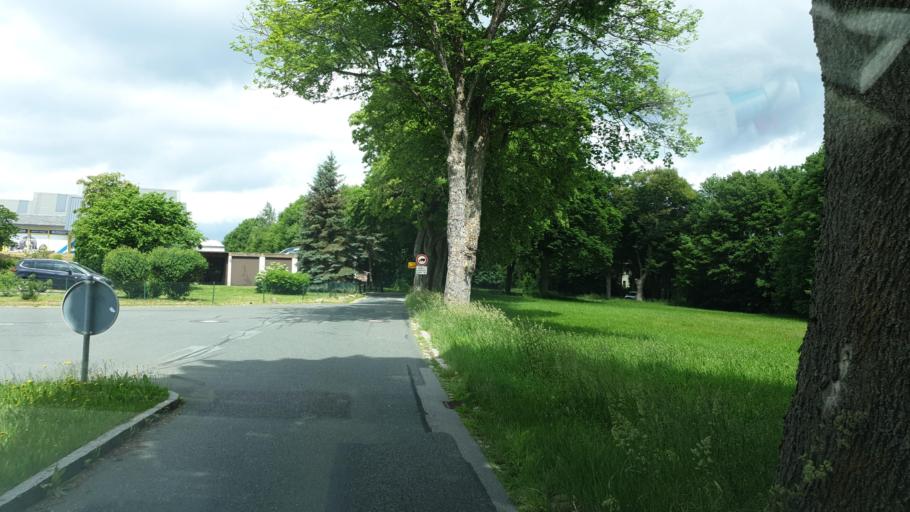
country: DE
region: Saxony
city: Marienberg
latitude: 50.6593
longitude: 13.1539
